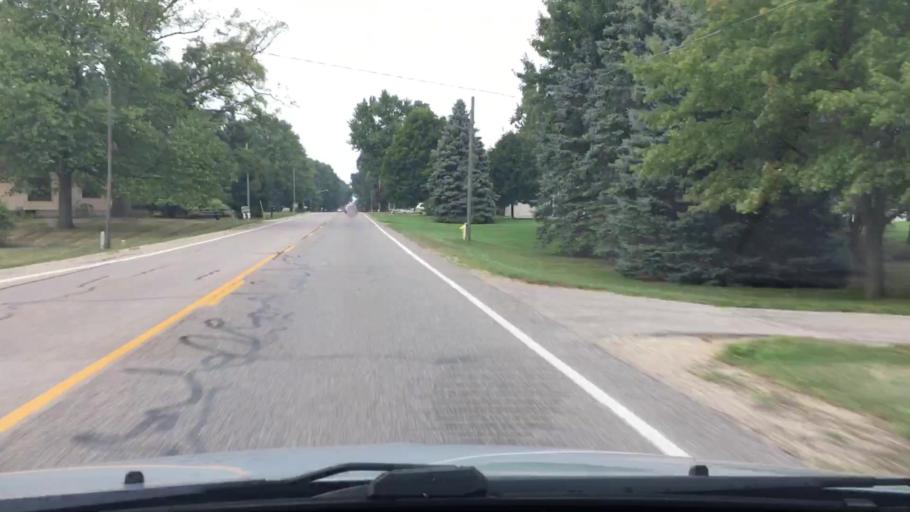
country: US
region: Michigan
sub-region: Ottawa County
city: Hudsonville
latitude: 42.8965
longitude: -85.9018
